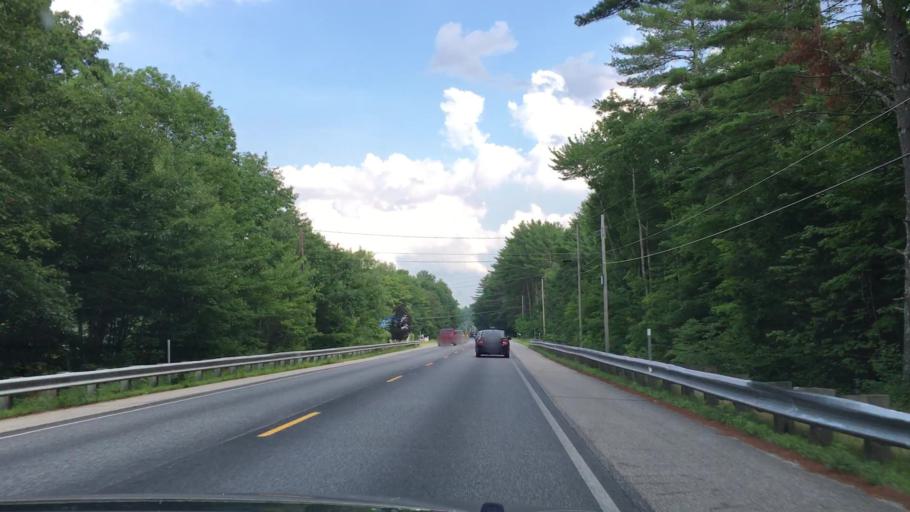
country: US
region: New Hampshire
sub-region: Strafford County
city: Farmington
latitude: 43.3917
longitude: -71.0918
